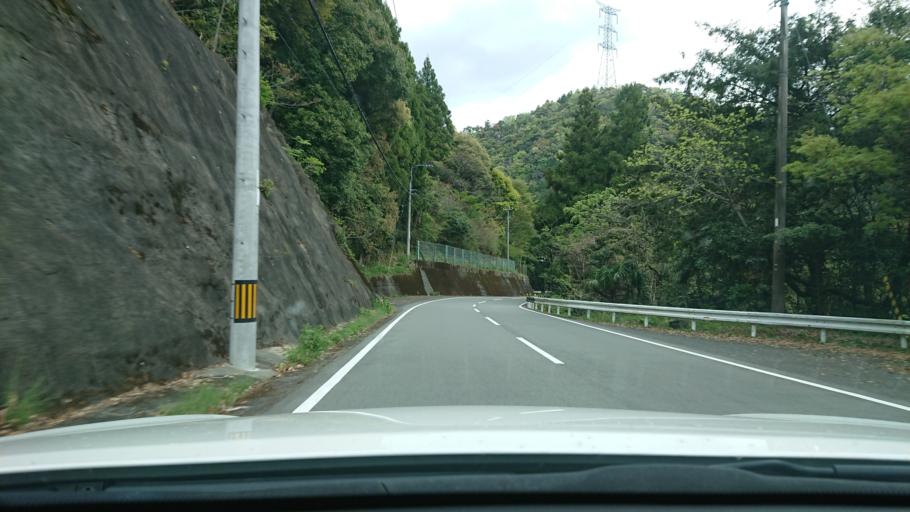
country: JP
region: Tokushima
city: Ishii
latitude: 33.9092
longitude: 134.4205
